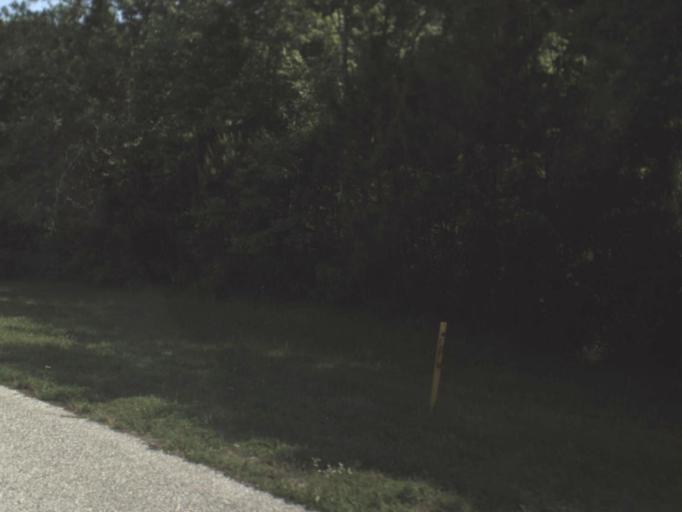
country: US
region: Florida
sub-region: Saint Johns County
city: Villano Beach
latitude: 29.9714
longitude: -81.3552
